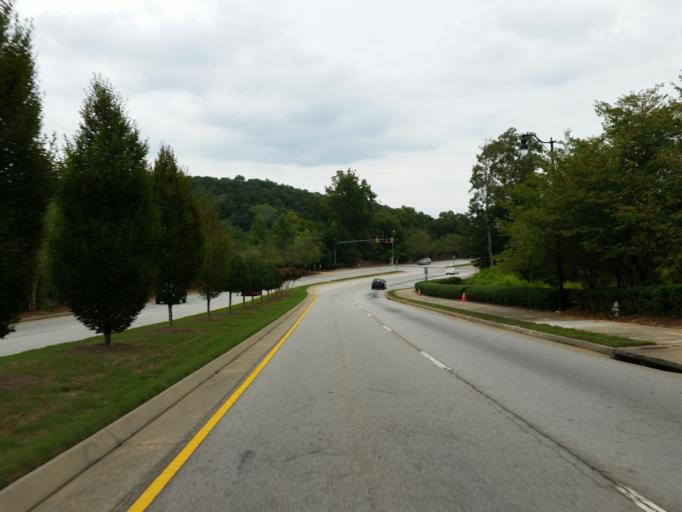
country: US
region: Georgia
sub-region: Cobb County
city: Vinings
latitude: 33.8850
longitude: -84.4533
